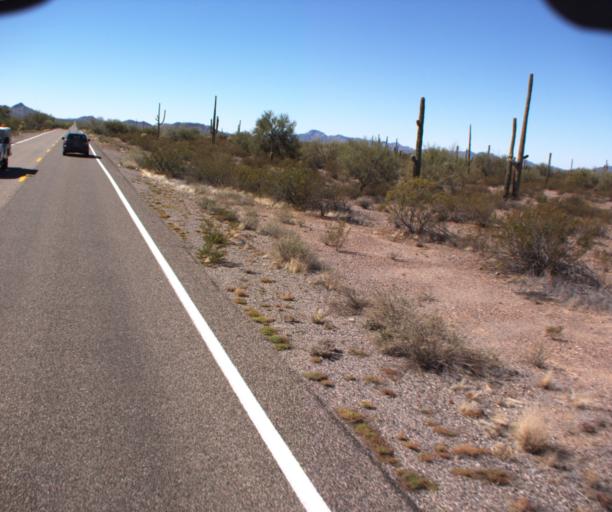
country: US
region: Arizona
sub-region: Pima County
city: Ajo
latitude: 32.1595
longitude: -112.7642
